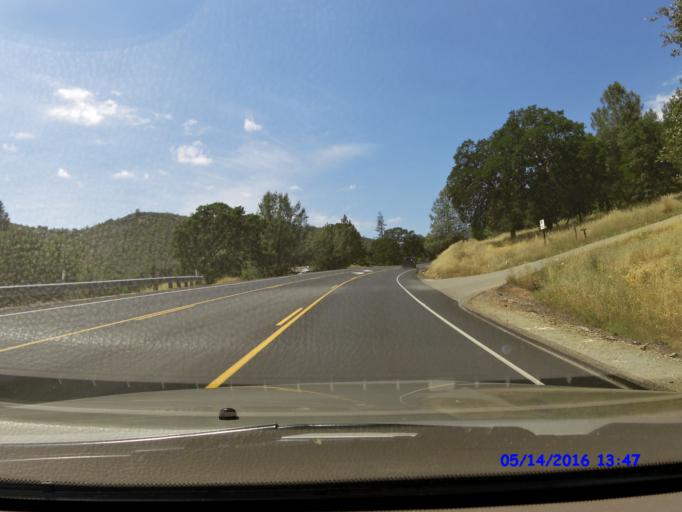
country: US
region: California
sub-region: Mariposa County
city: Mariposa
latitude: 37.4932
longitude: -119.9764
